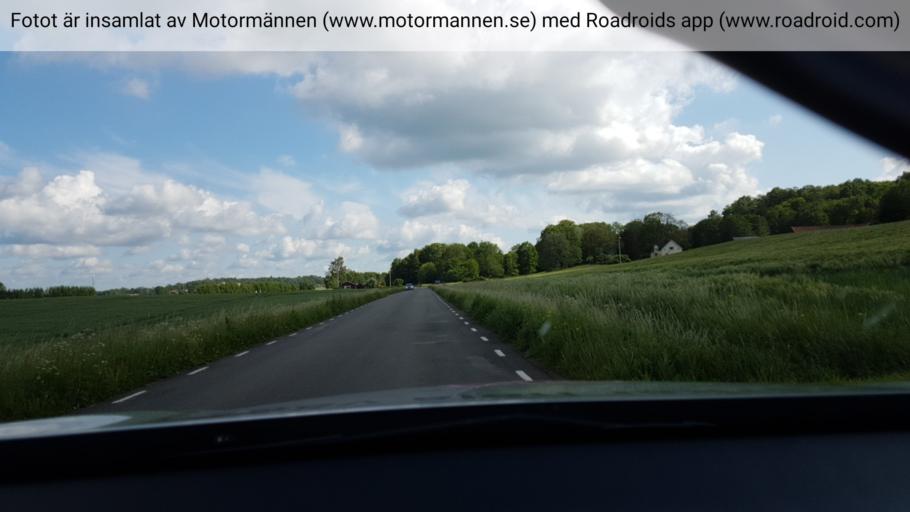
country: SE
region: Vaestra Goetaland
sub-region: Skara Kommun
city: Axvall
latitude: 58.3585
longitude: 13.6242
